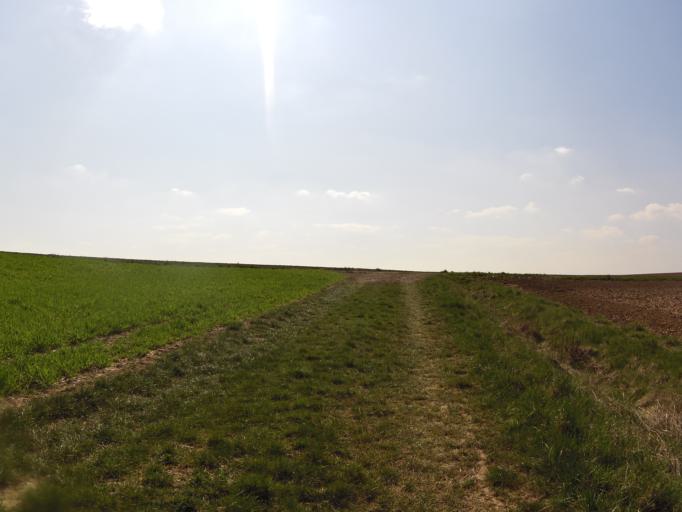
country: DE
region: Bavaria
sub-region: Regierungsbezirk Unterfranken
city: Dettelbach
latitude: 49.8159
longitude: 10.1392
